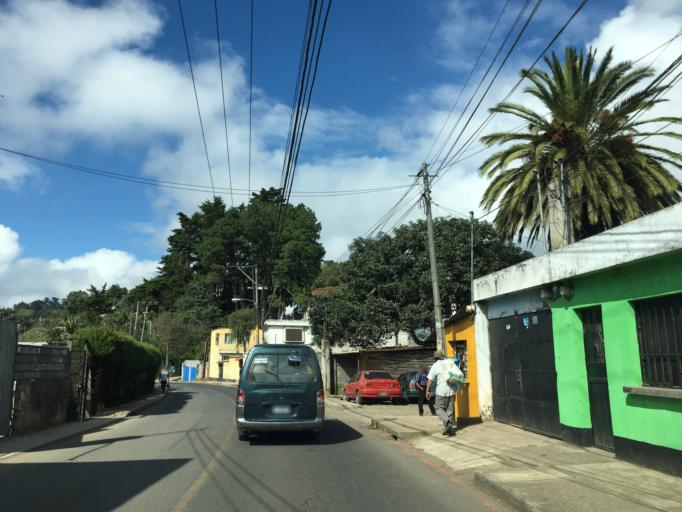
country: GT
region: Guatemala
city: San Jose Pinula
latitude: 14.5523
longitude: -90.4375
